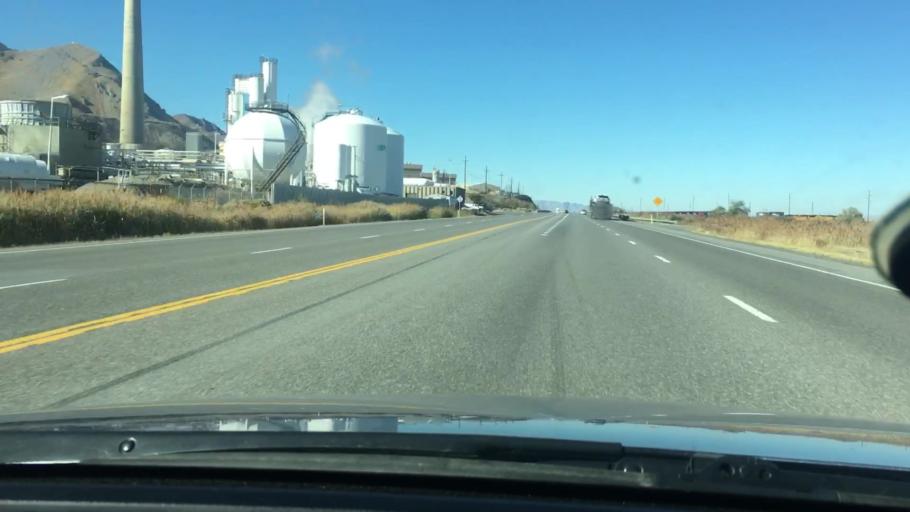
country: US
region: Utah
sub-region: Salt Lake County
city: Magna
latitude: 40.7276
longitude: -112.1843
